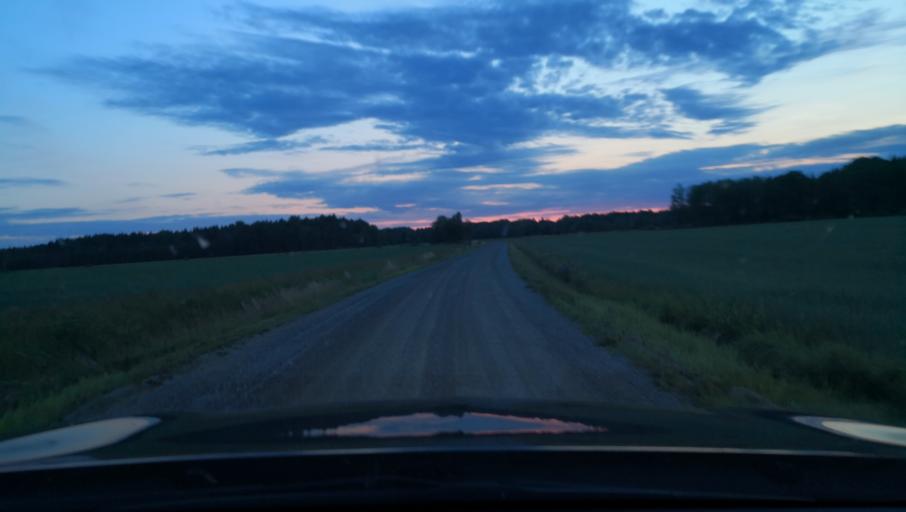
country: SE
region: Uppsala
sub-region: Heby Kommun
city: OEstervala
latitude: 60.0129
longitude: 17.3112
